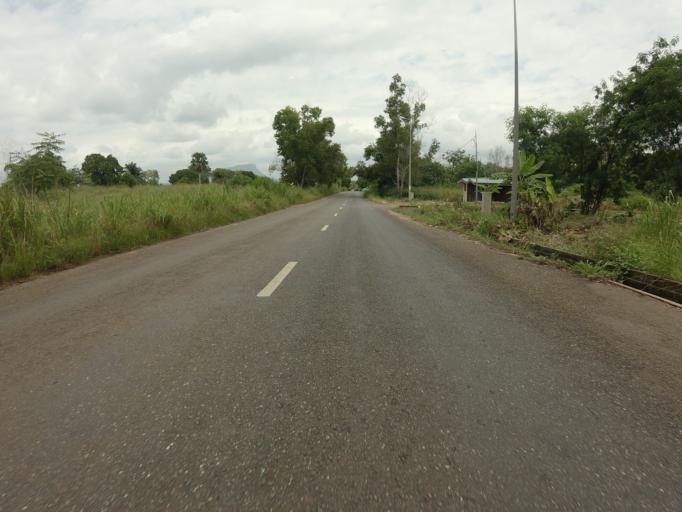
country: GH
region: Volta
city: Ho
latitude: 6.5909
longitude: 0.4626
